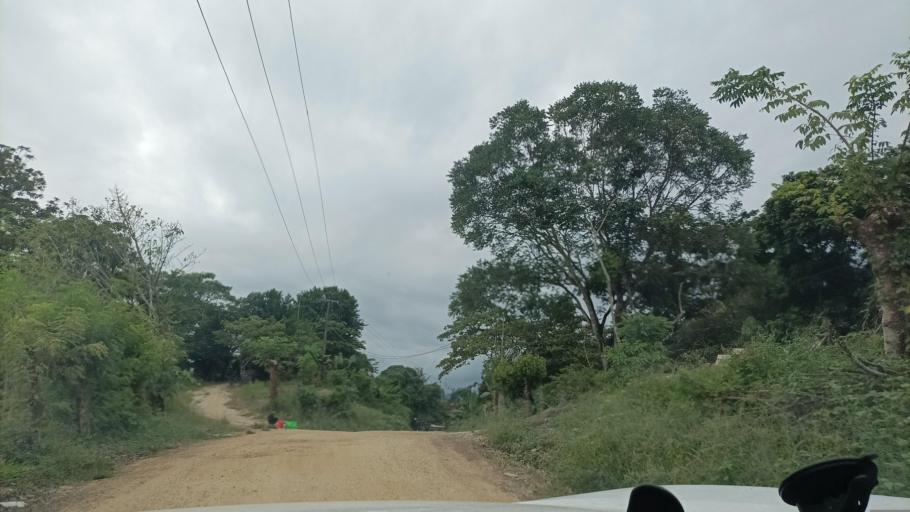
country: MX
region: Veracruz
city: Hidalgotitlan
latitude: 17.6362
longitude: -94.5122
